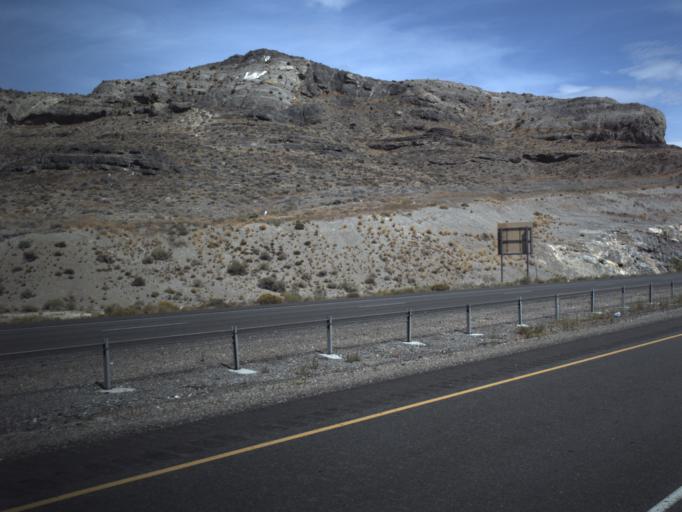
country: US
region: Utah
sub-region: Tooele County
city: Wendover
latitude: 40.7411
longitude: -114.0321
